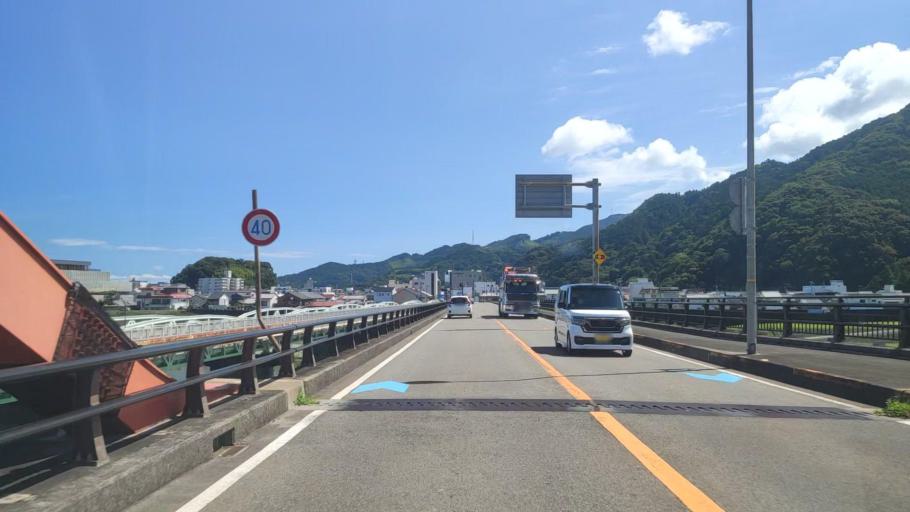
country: JP
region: Wakayama
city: Shingu
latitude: 33.7335
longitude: 135.9877
